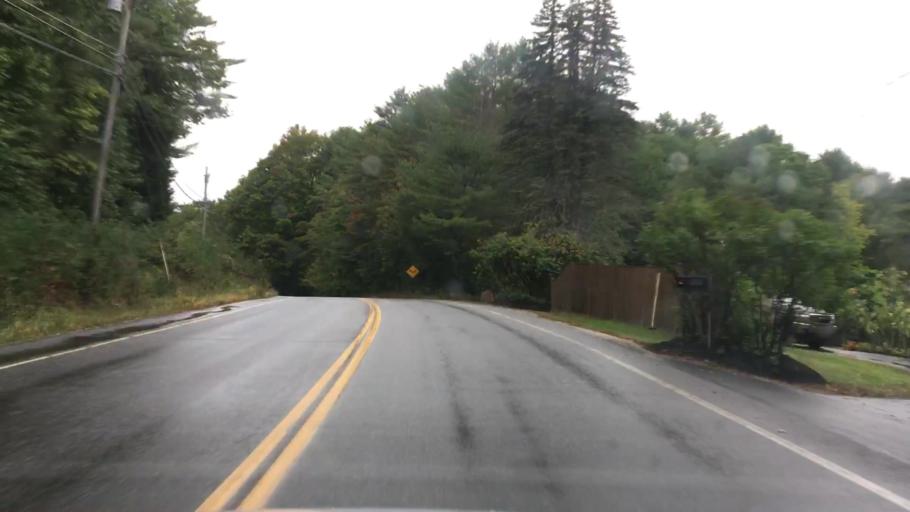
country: US
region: Maine
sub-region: Cumberland County
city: Raymond
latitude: 43.9848
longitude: -70.5096
